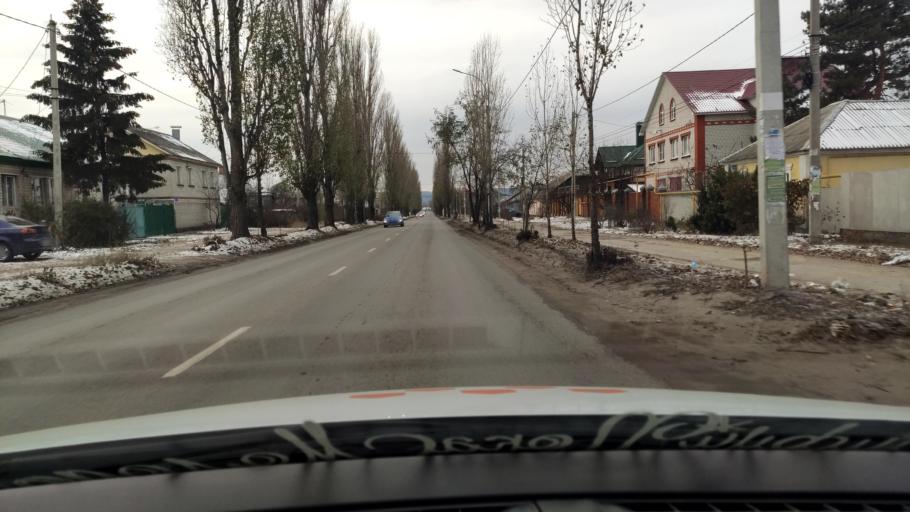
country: RU
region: Voronezj
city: Somovo
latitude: 51.7392
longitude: 39.2769
